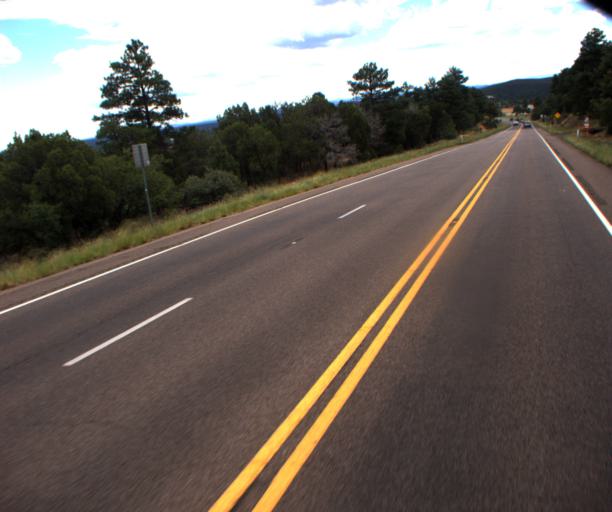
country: US
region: Arizona
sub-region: Navajo County
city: Linden
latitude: 34.2886
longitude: -110.1746
